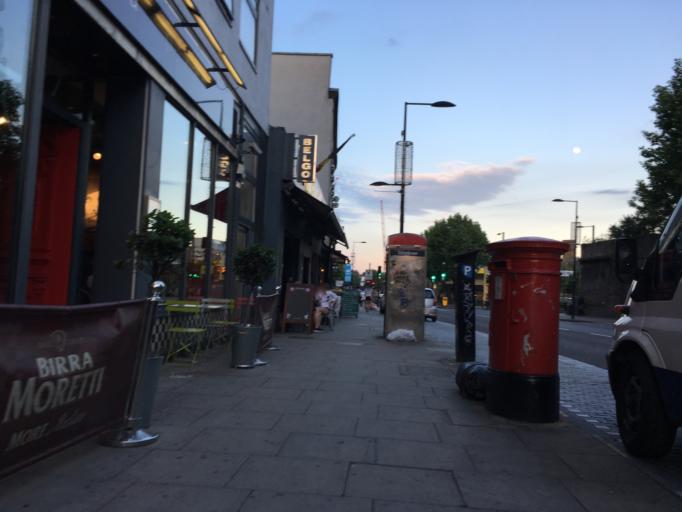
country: GB
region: England
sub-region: Greater London
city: Camden Town
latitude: 51.5434
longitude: -0.1511
